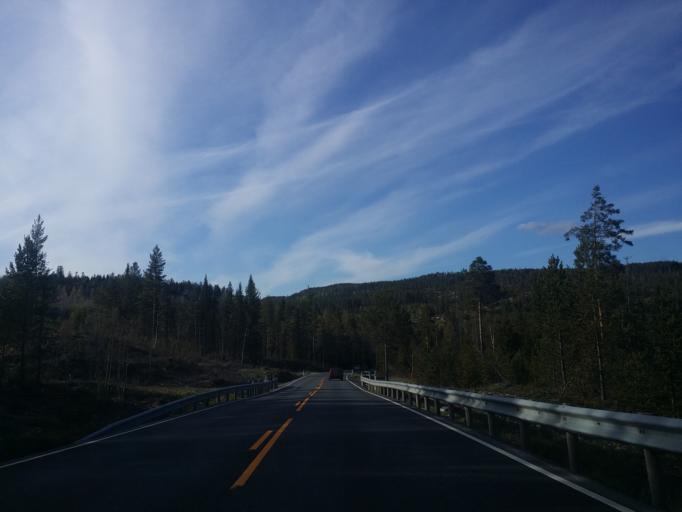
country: NO
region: Buskerud
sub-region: Kongsberg
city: Kongsberg
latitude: 59.6227
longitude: 9.4738
